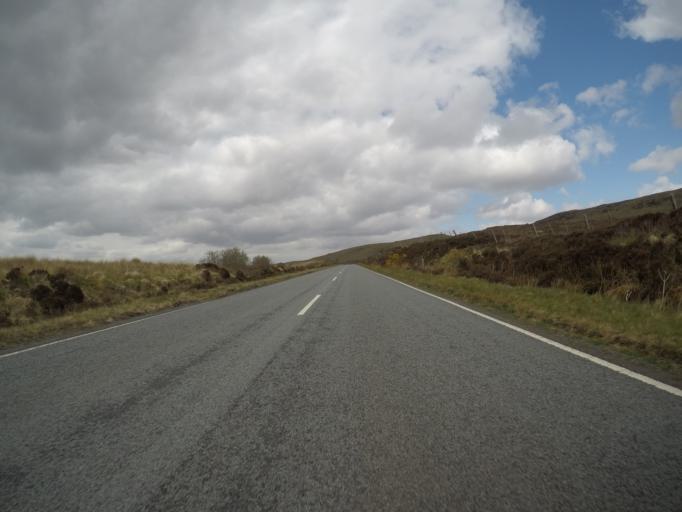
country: GB
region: Scotland
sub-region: Highland
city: Isle of Skye
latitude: 57.3126
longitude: -6.3195
